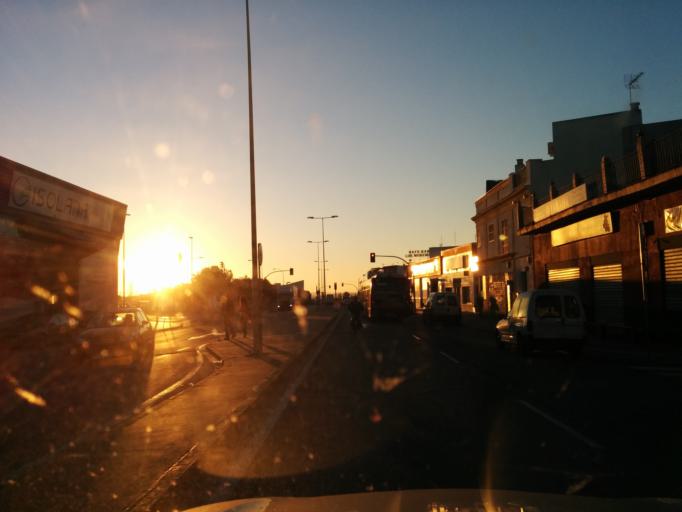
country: ES
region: Andalusia
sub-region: Provincia de Sevilla
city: Sevilla
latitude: 37.3761
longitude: -5.9315
